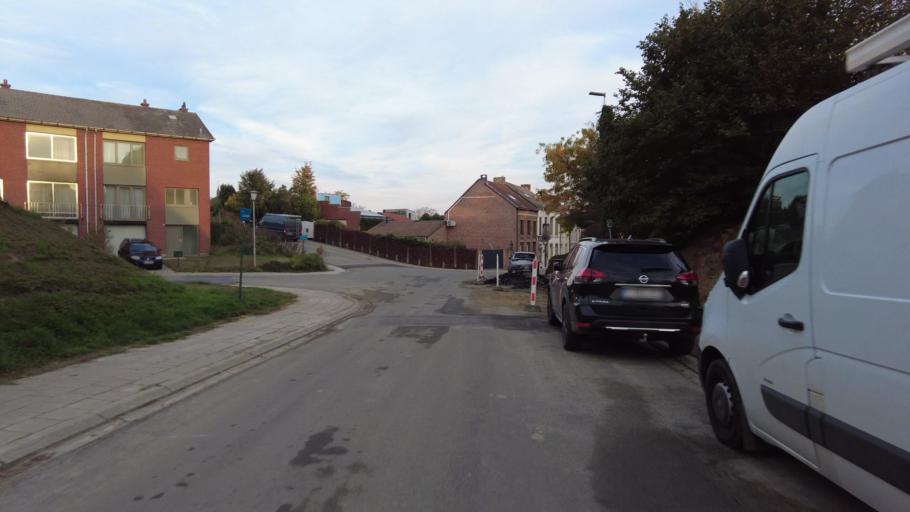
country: BE
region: Wallonia
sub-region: Province du Brabant Wallon
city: Jodoigne
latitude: 50.7250
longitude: 4.8619
